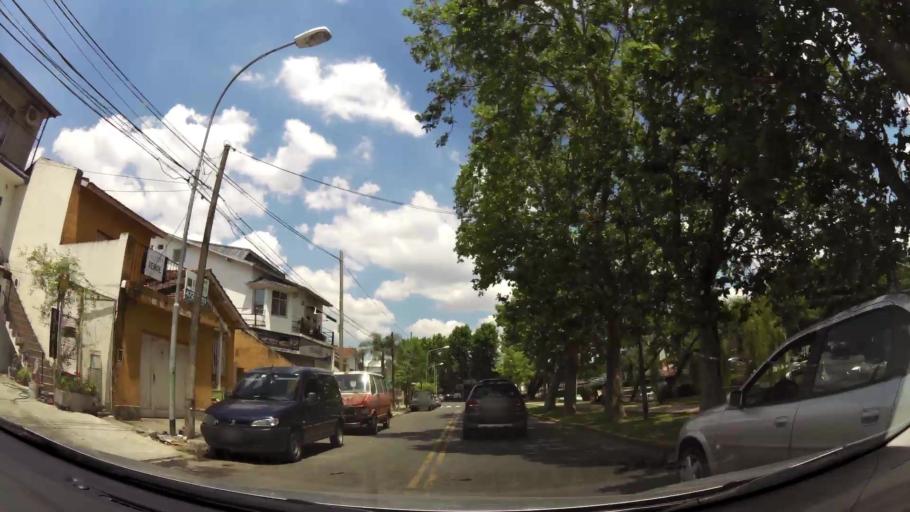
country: AR
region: Buenos Aires
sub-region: Partido de Tigre
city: Tigre
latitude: -34.4099
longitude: -58.5923
